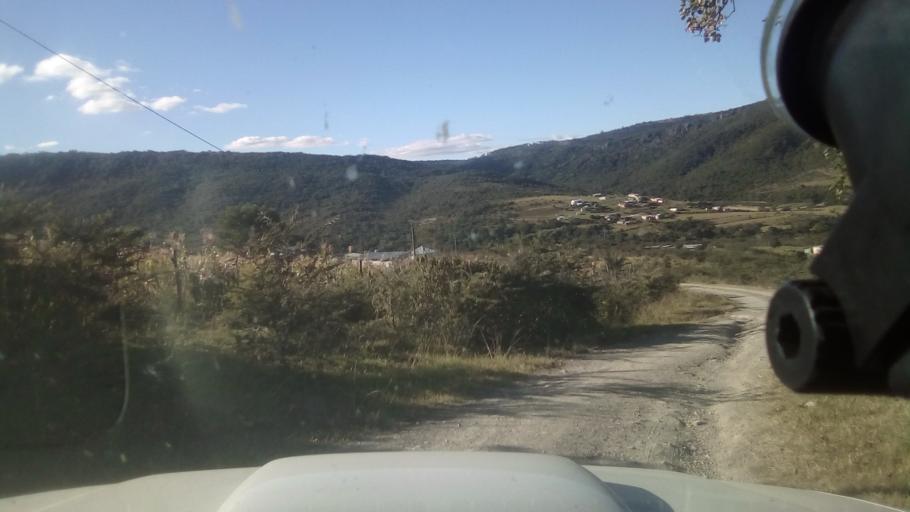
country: ZA
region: Eastern Cape
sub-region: Buffalo City Metropolitan Municipality
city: Bhisho
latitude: -32.7322
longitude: 27.3469
